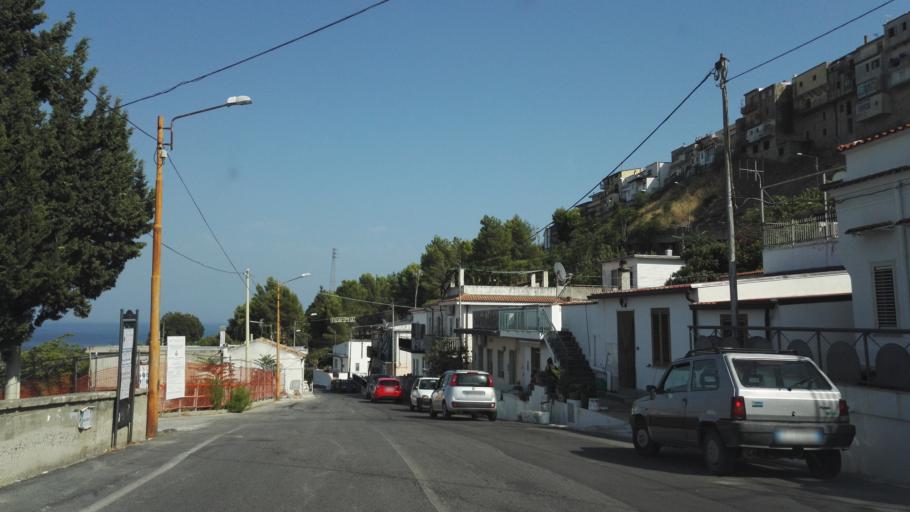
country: IT
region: Calabria
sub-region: Provincia di Reggio Calabria
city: Monasterace
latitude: 38.4548
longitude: 16.5522
